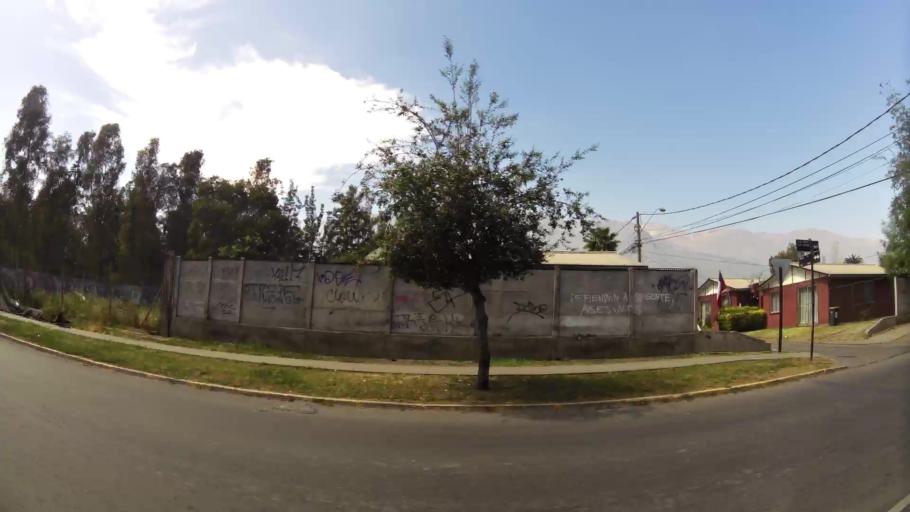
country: CL
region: Santiago Metropolitan
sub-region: Provincia de Santiago
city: Villa Presidente Frei, Nunoa, Santiago, Chile
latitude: -33.4620
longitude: -70.5415
